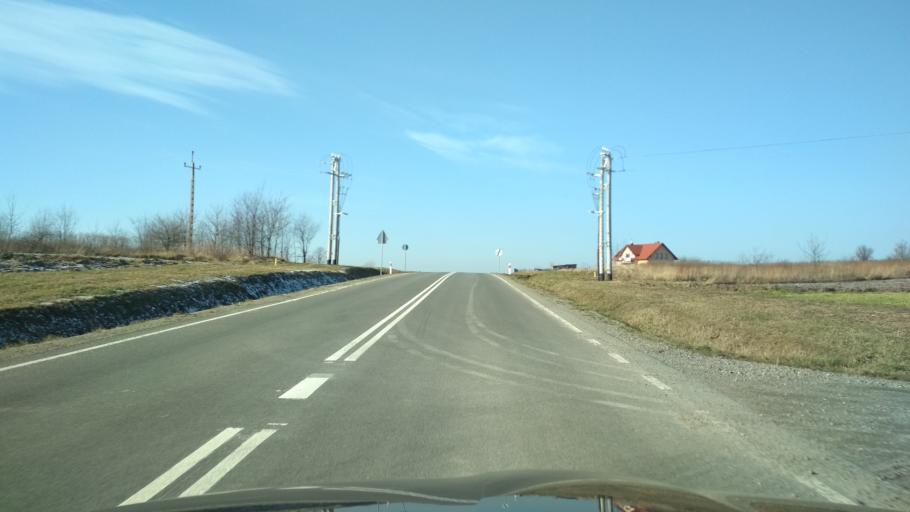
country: PL
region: Subcarpathian Voivodeship
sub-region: Powiat ropczycko-sedziszowski
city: Sedziszow Malopolski
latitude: 50.0764
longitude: 21.7266
